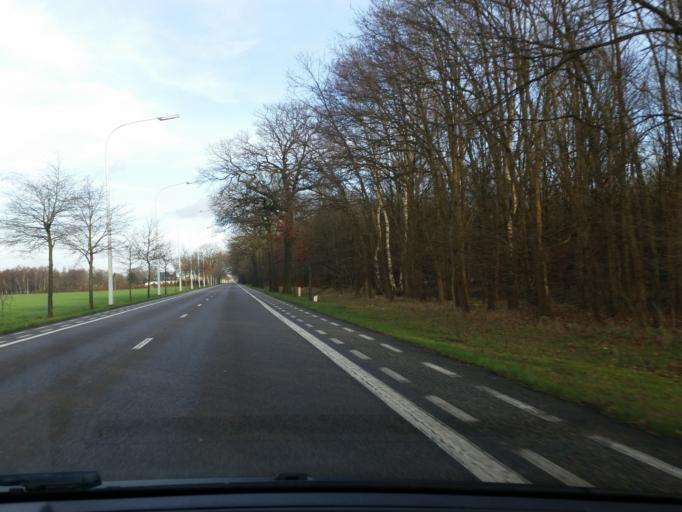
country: BE
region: Flanders
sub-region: Provincie Antwerpen
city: Wuustwezel
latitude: 51.3704
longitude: 4.5677
